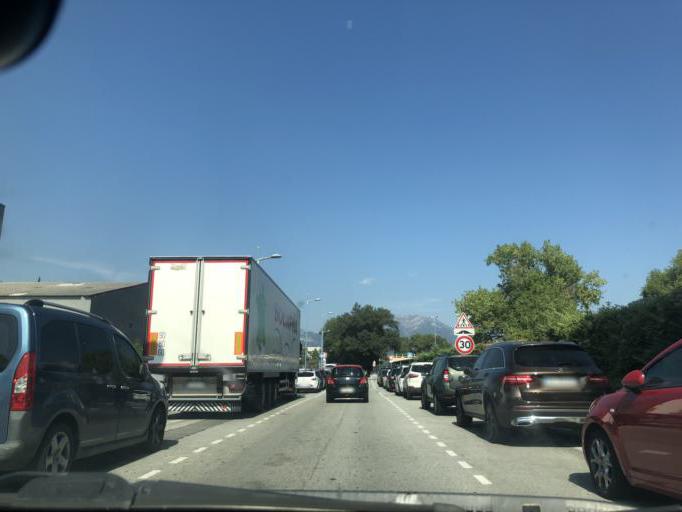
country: FR
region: Provence-Alpes-Cote d'Azur
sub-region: Departement des Alpes-Maritimes
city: Castagniers
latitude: 43.7848
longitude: 7.2116
